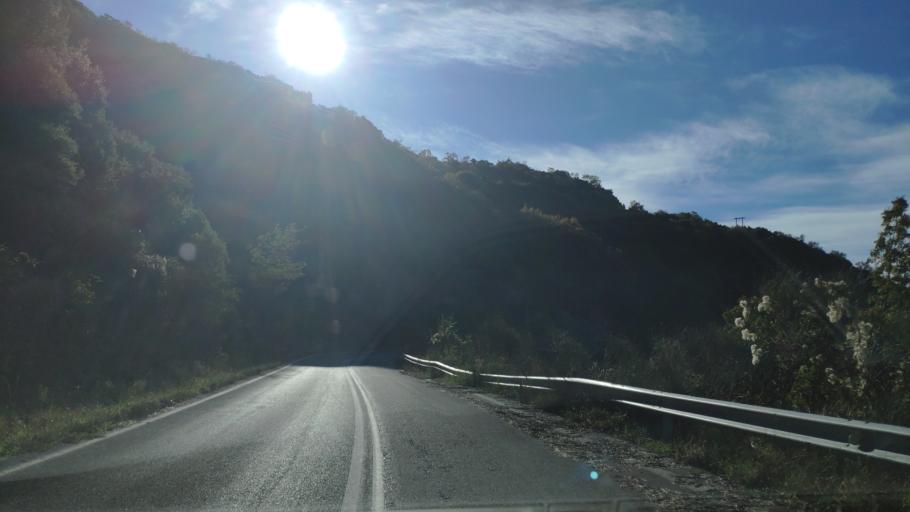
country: GR
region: Peloponnese
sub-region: Nomos Arkadias
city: Dimitsana
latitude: 37.5641
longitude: 22.0623
